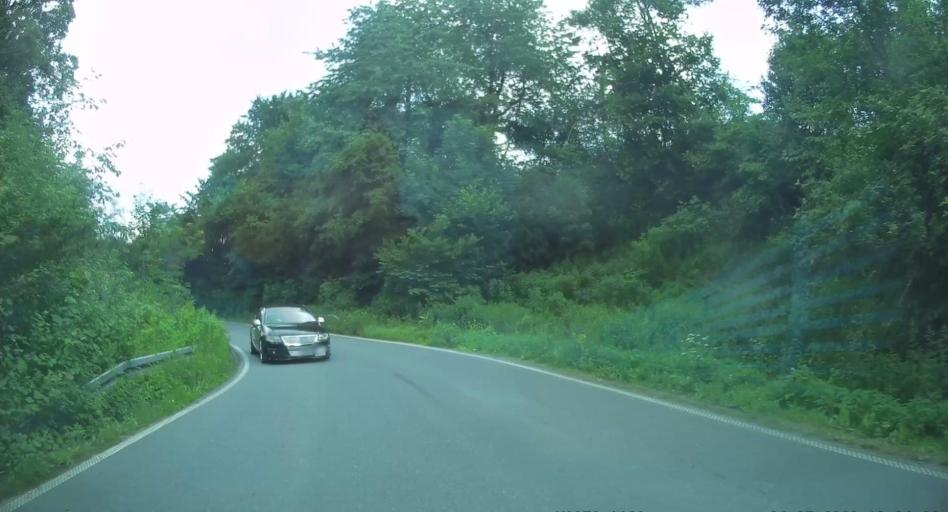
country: PL
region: Lesser Poland Voivodeship
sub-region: Powiat nowosadecki
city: Korzenna
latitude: 49.7205
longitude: 20.7746
